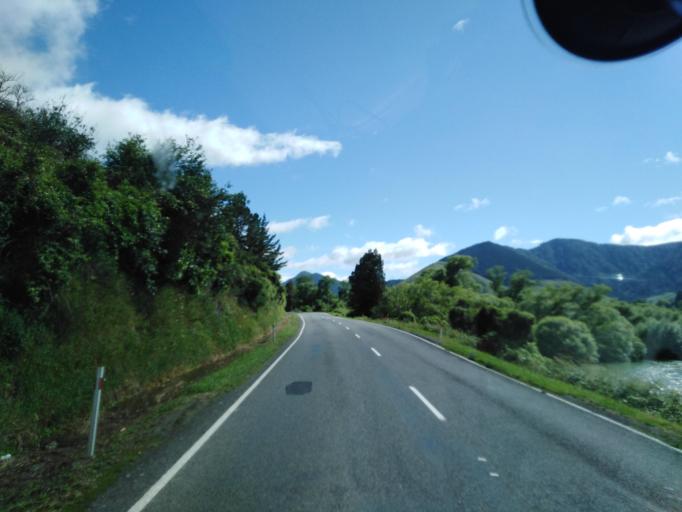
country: NZ
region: Nelson
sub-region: Nelson City
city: Nelson
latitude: -41.2550
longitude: 173.5766
